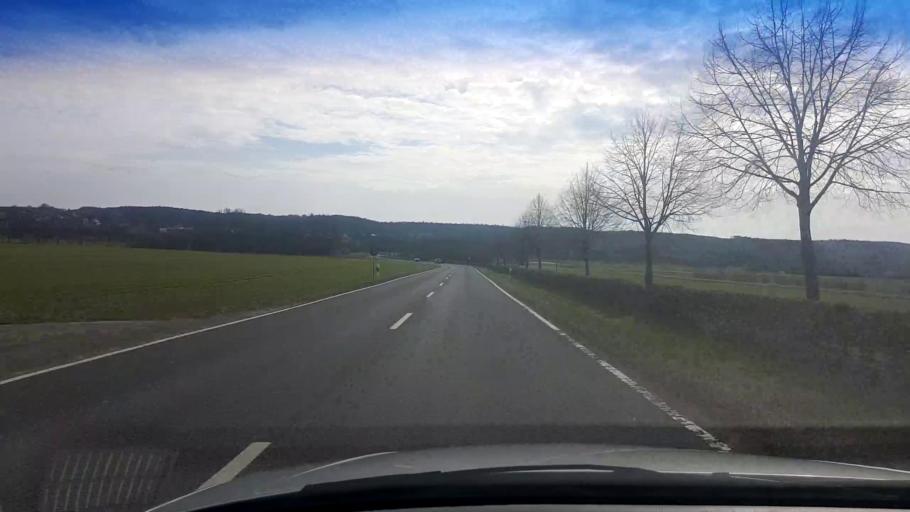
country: DE
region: Bavaria
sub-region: Upper Franconia
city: Frensdorf
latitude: 49.8256
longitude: 10.8662
